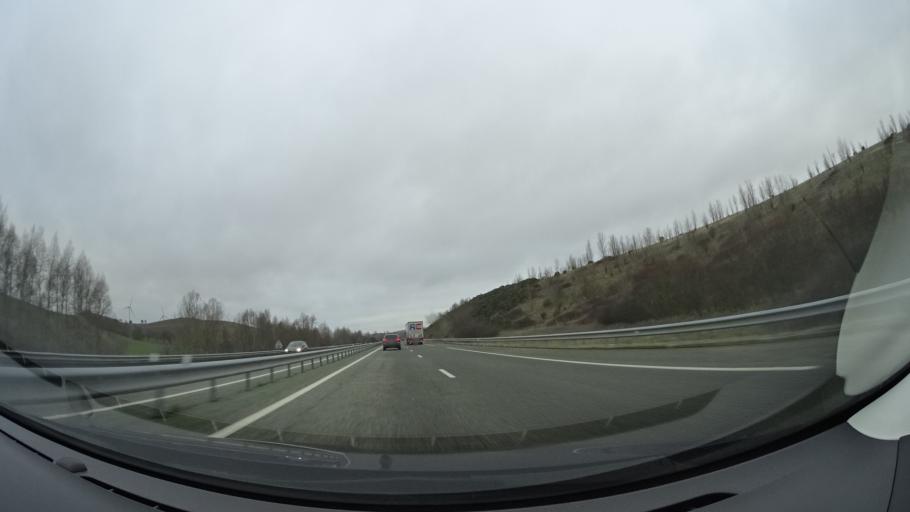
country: FR
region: Midi-Pyrenees
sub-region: Departement de la Haute-Garonne
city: Calmont
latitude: 43.3180
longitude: 1.6433
